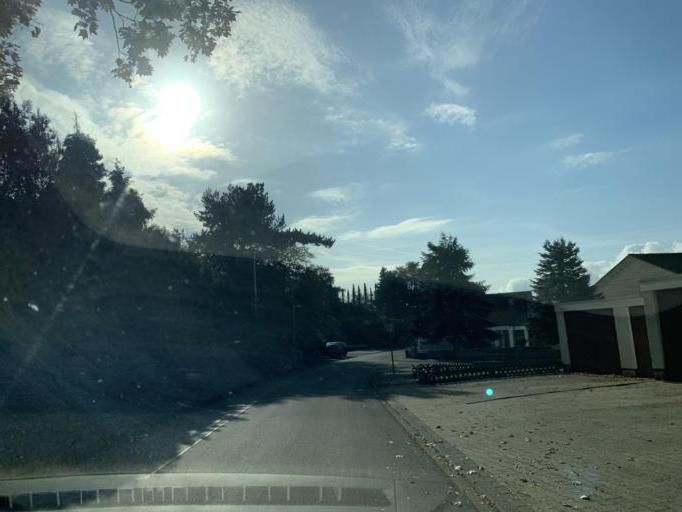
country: DE
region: North Rhine-Westphalia
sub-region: Regierungsbezirk Koln
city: Dueren
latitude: 50.8230
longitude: 6.4768
